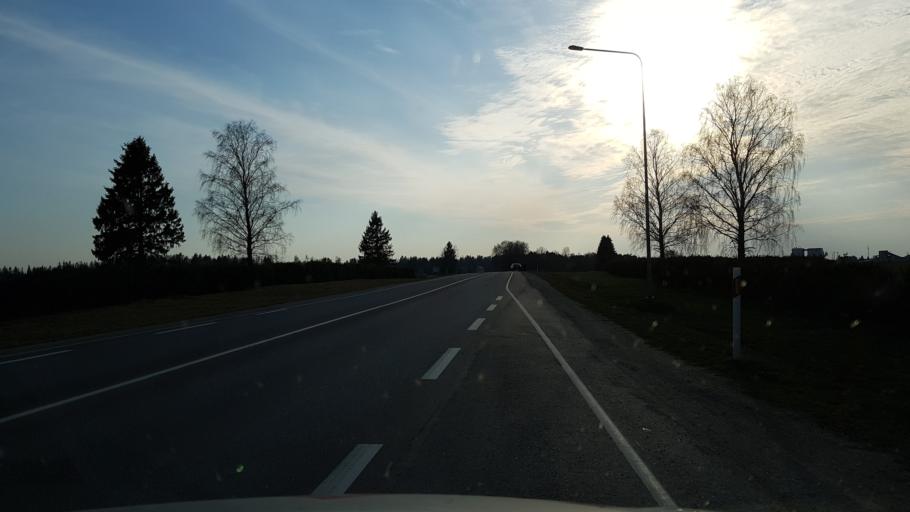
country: EE
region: Laeaene-Virumaa
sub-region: Someru vald
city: Someru
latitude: 59.3656
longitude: 26.4298
